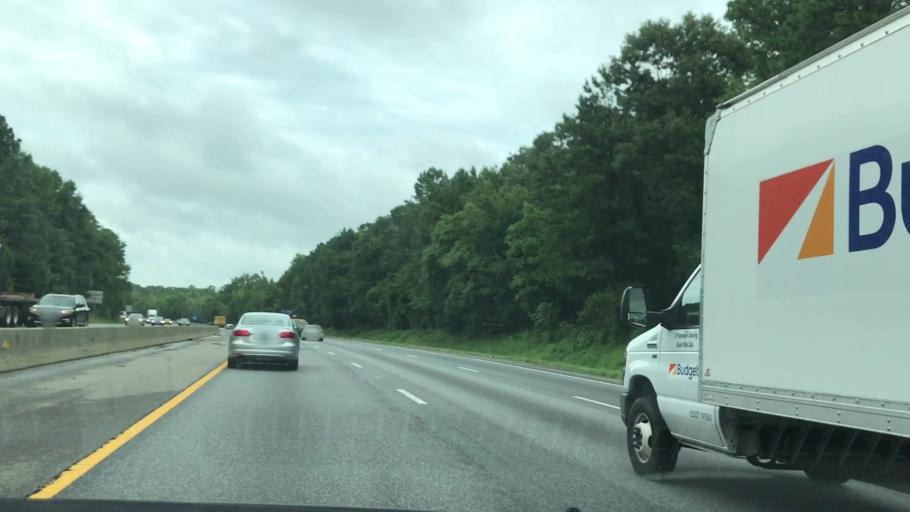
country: US
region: Virginia
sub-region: City of Colonial Heights
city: Colonial Heights
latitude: 37.2808
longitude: -77.3888
